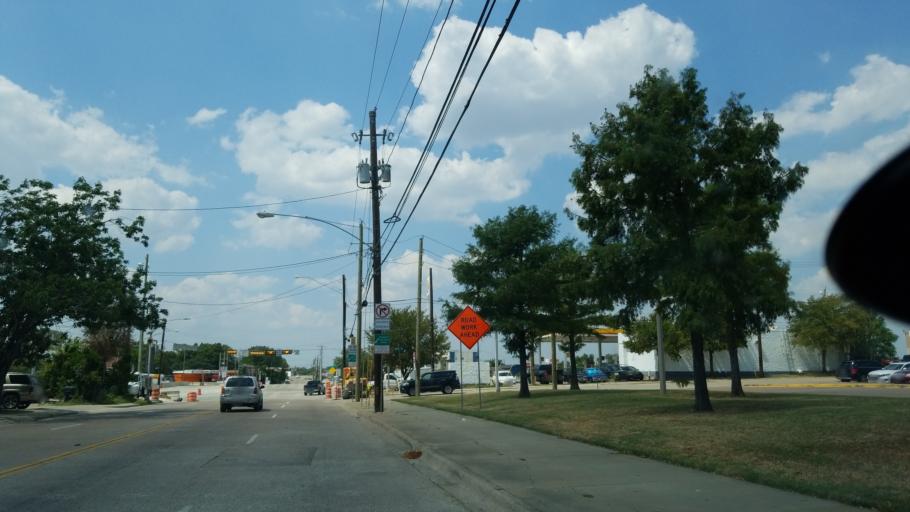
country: US
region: Texas
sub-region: Dallas County
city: Dallas
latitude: 32.7513
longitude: -96.8077
